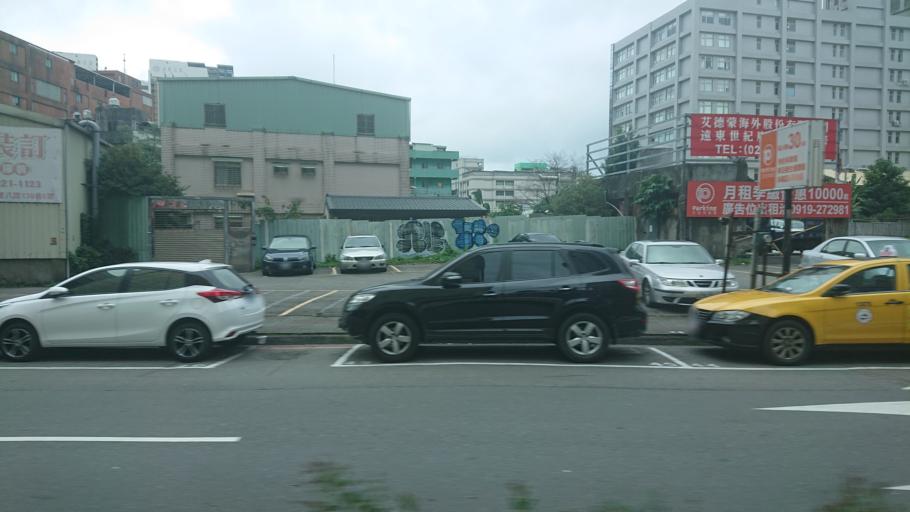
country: TW
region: Taipei
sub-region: Taipei
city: Banqiao
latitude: 24.9976
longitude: 121.4882
